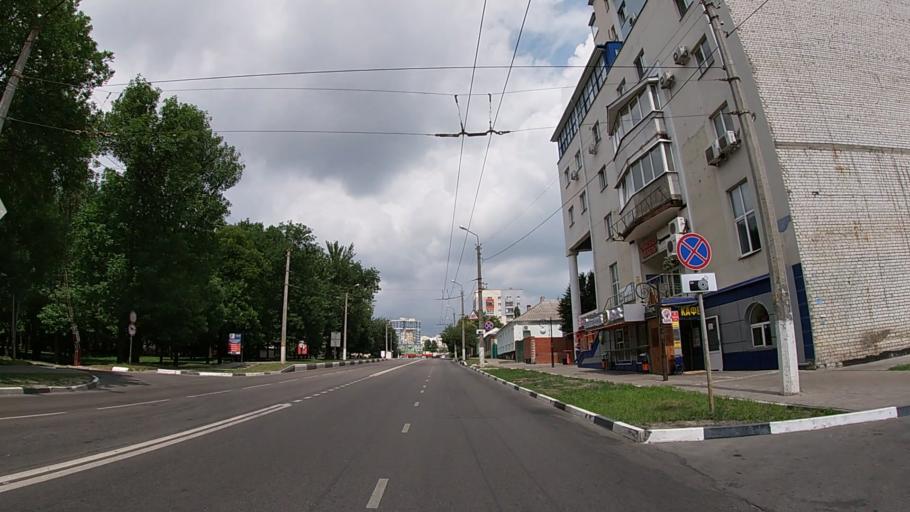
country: RU
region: Belgorod
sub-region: Belgorodskiy Rayon
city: Belgorod
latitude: 50.6074
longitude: 36.5915
